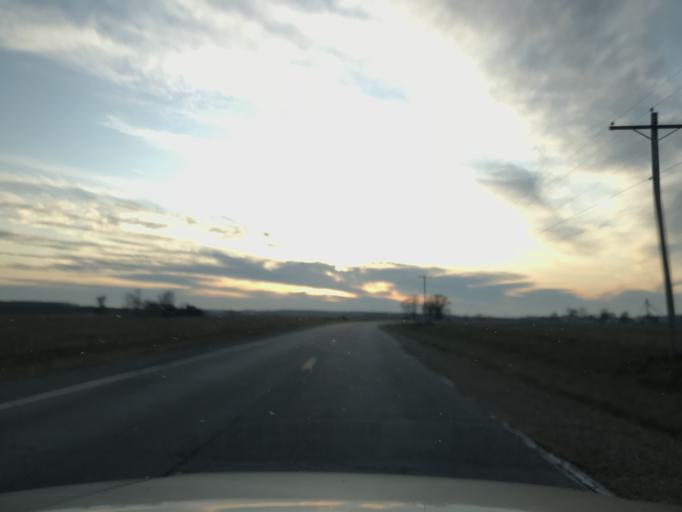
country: US
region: Illinois
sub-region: Warren County
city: Monmouth
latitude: 41.0198
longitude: -90.7902
